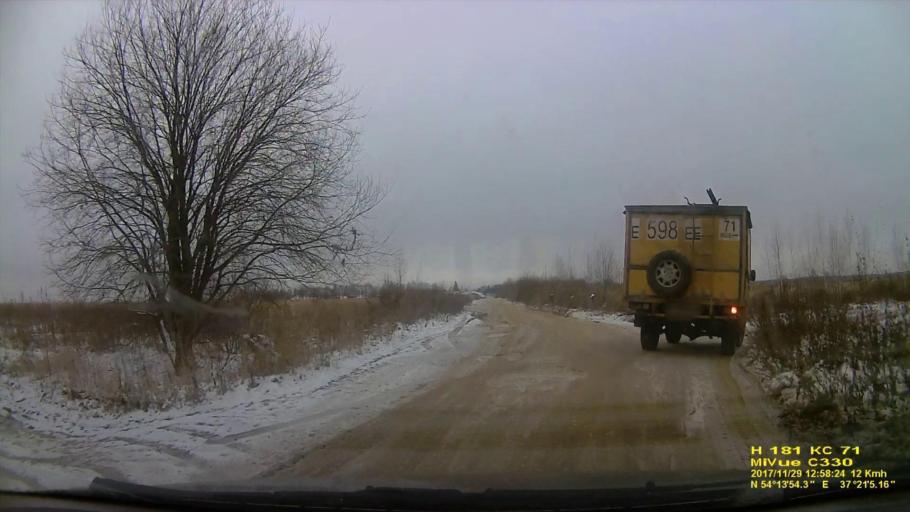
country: RU
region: Tula
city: Leninskiy
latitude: 54.2318
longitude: 37.3516
